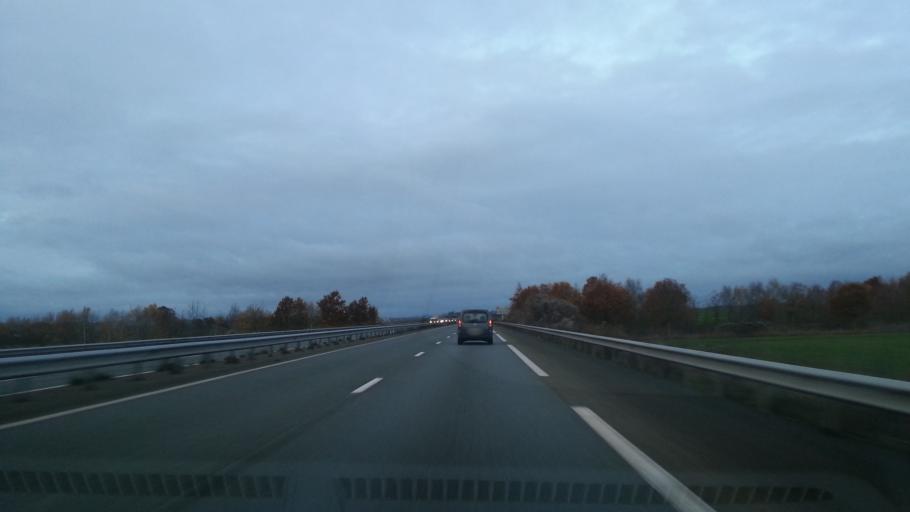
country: FR
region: Picardie
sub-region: Departement de l'Oise
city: Bresles
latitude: 49.4124
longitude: 2.3203
